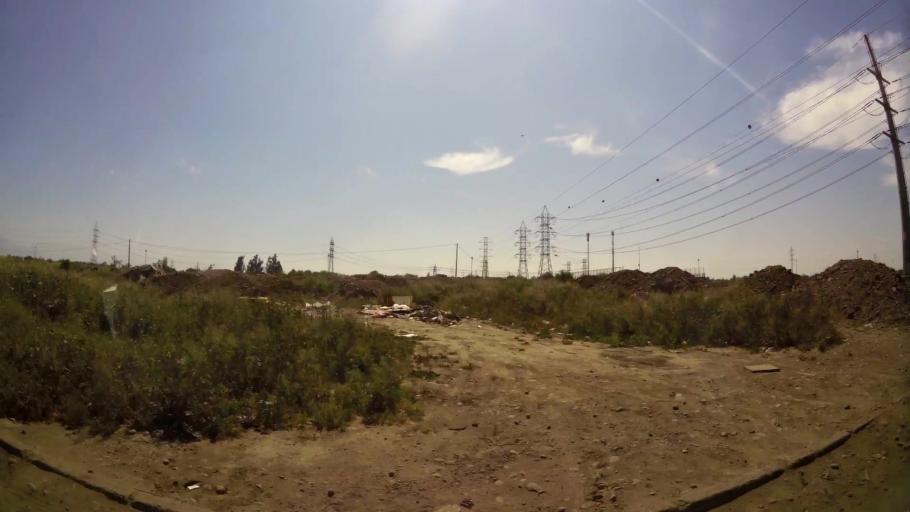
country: CL
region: Santiago Metropolitan
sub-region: Provincia de Santiago
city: Lo Prado
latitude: -33.4853
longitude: -70.7320
